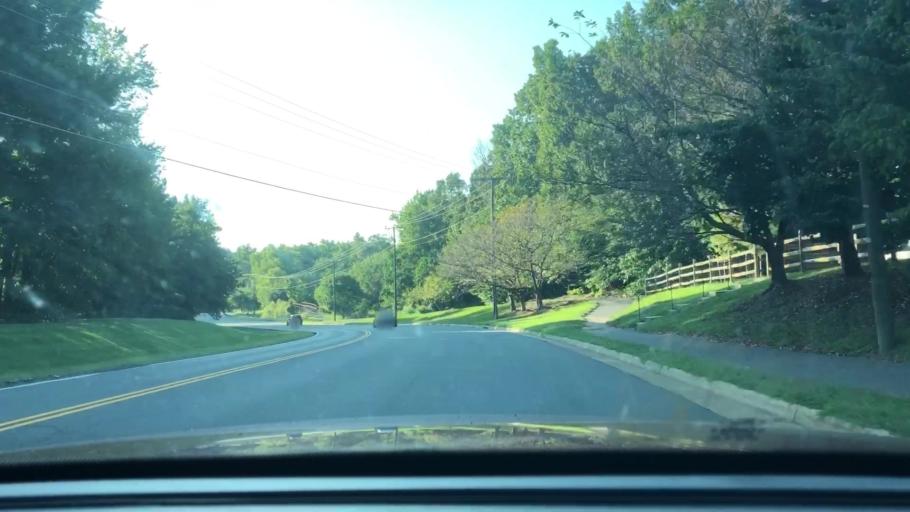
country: US
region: Virginia
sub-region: Fairfax County
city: Centreville
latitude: 38.8336
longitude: -77.4158
